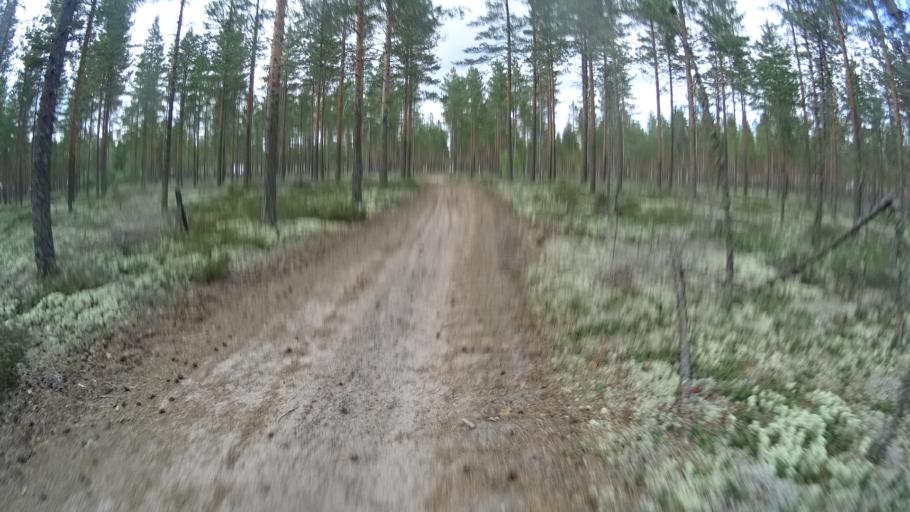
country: FI
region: Satakunta
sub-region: Pohjois-Satakunta
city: Jaemijaervi
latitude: 61.7683
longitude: 22.8026
